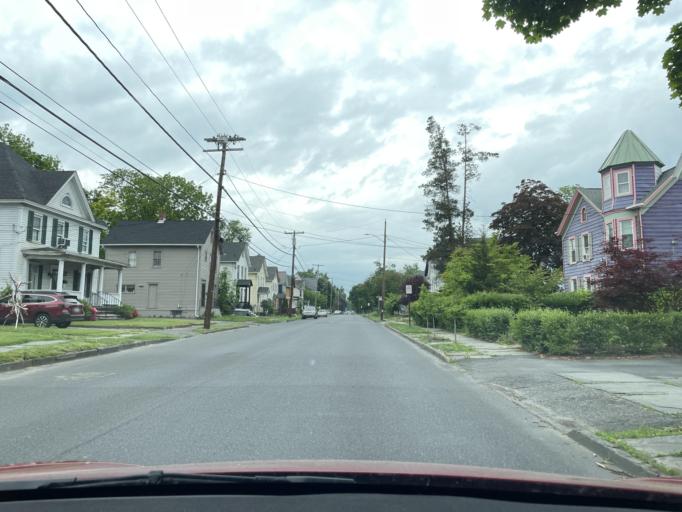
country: US
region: New York
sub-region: Ulster County
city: Kingston
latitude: 41.9275
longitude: -74.0182
